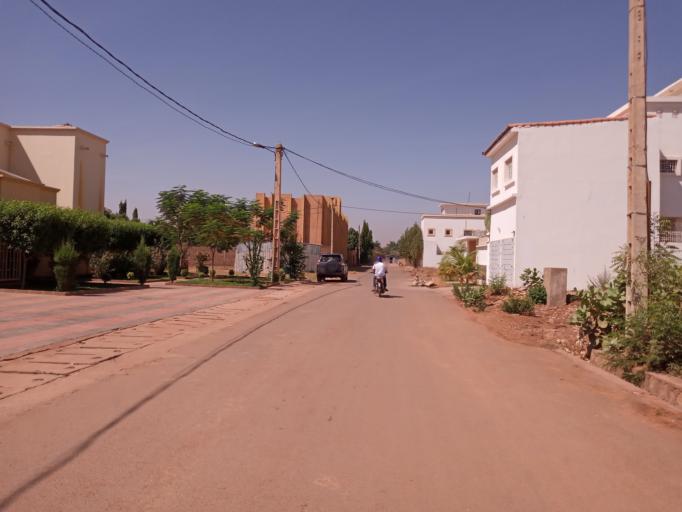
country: ML
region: Bamako
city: Bamako
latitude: 12.6032
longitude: -8.0471
